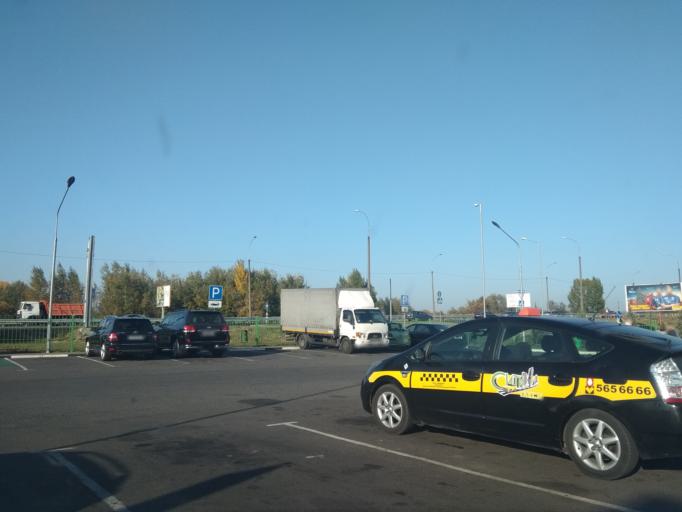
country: BY
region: Brest
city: Brest
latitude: 52.0772
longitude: 23.7236
